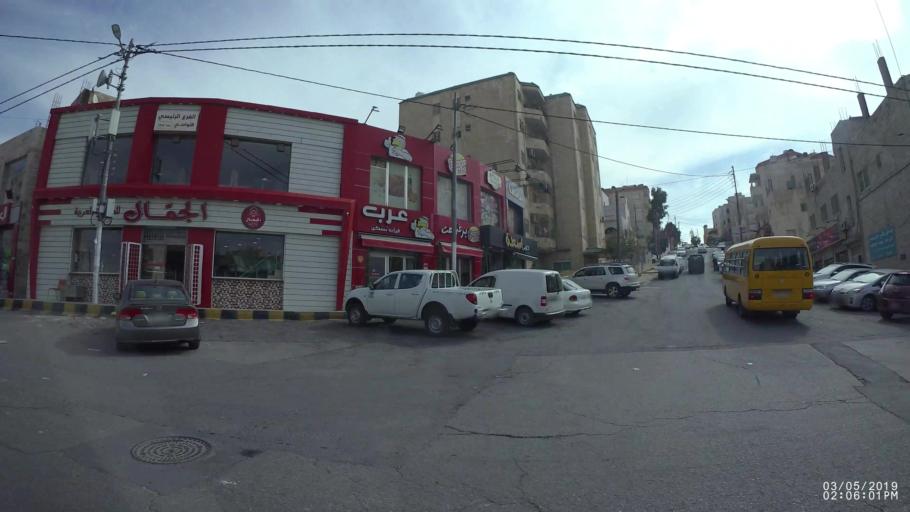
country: JO
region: Amman
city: Amman
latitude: 32.0031
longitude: 35.9386
